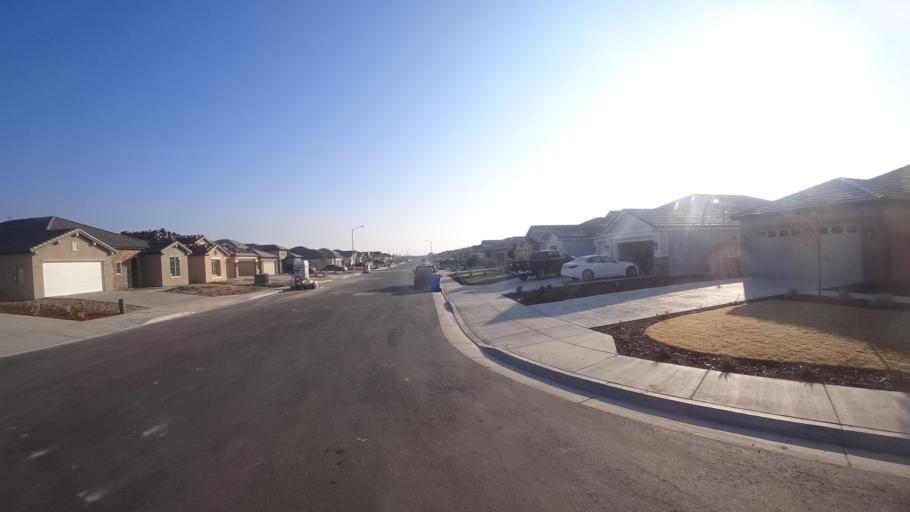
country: US
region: California
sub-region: Kern County
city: Greenacres
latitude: 35.2938
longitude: -119.1141
